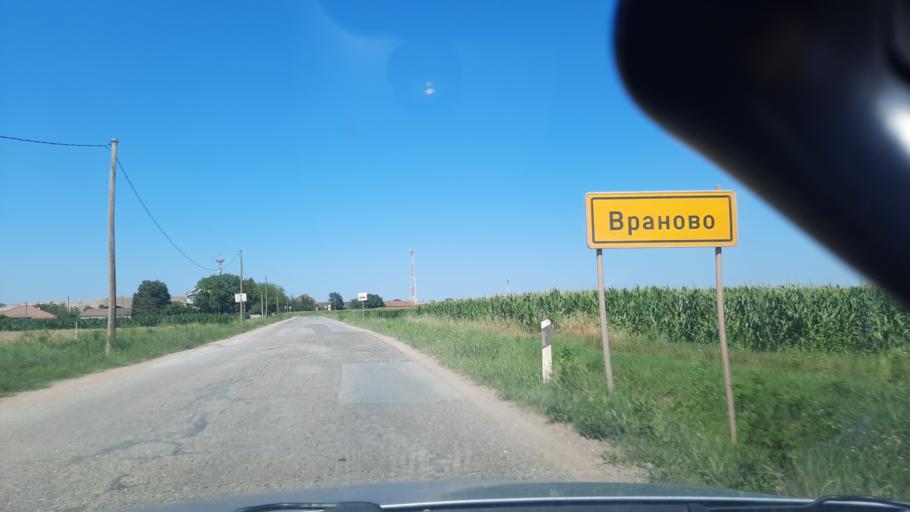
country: RS
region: Central Serbia
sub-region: Podunavski Okrug
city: Smederevo
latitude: 44.5916
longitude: 20.9821
